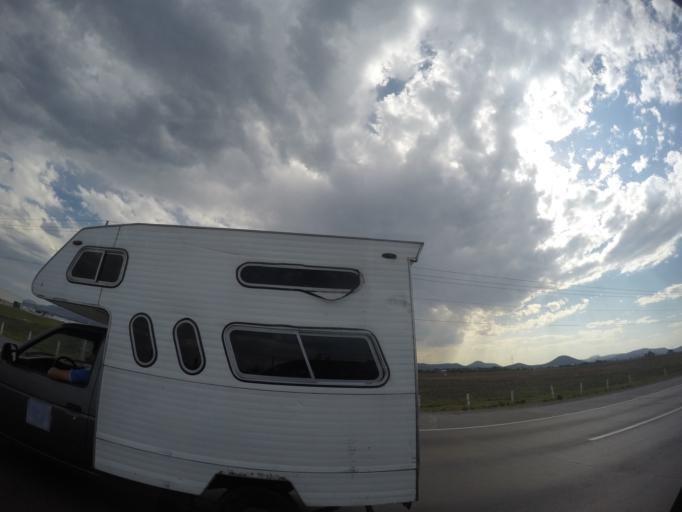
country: MX
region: Queretaro
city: La Estancia
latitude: 20.4385
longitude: -100.0691
